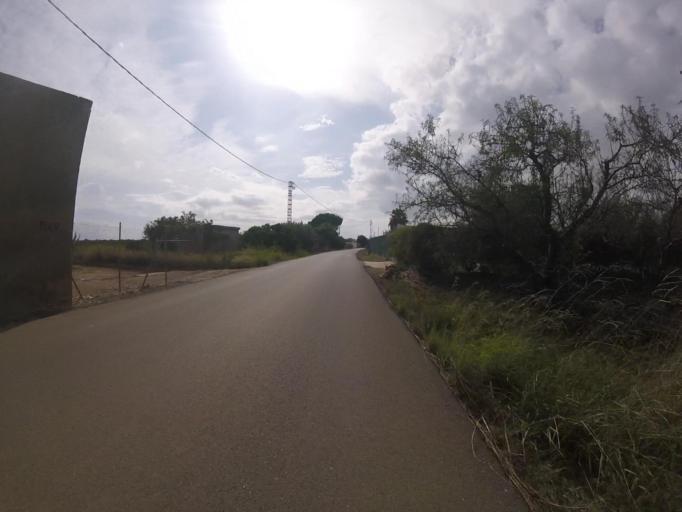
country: ES
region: Valencia
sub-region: Provincia de Castello
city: Orpesa/Oropesa del Mar
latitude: 40.1463
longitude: 0.1608
